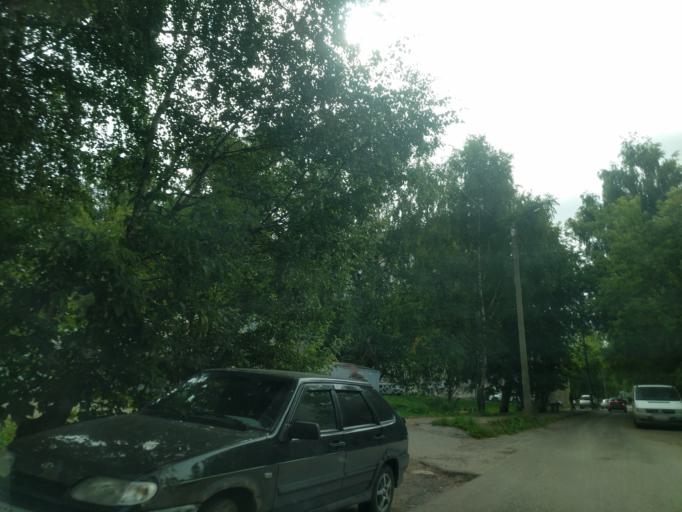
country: RU
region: Kirov
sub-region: Kirovo-Chepetskiy Rayon
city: Kirov
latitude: 58.5970
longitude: 49.6452
